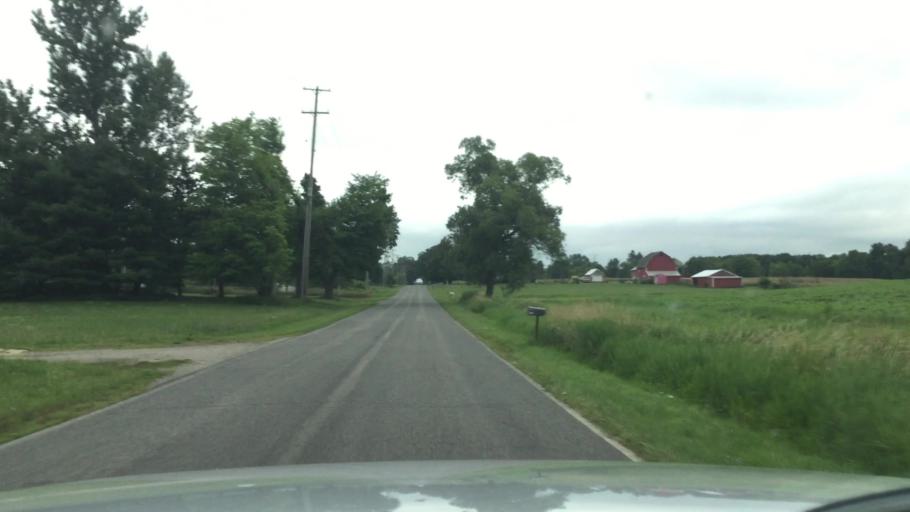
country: US
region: Michigan
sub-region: Montcalm County
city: Greenville
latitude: 43.1854
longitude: -85.2232
